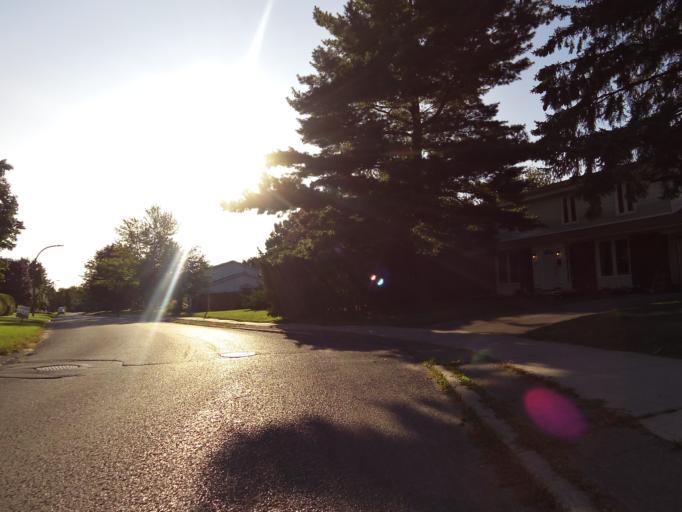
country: CA
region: Ontario
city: Ottawa
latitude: 45.3540
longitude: -75.7198
